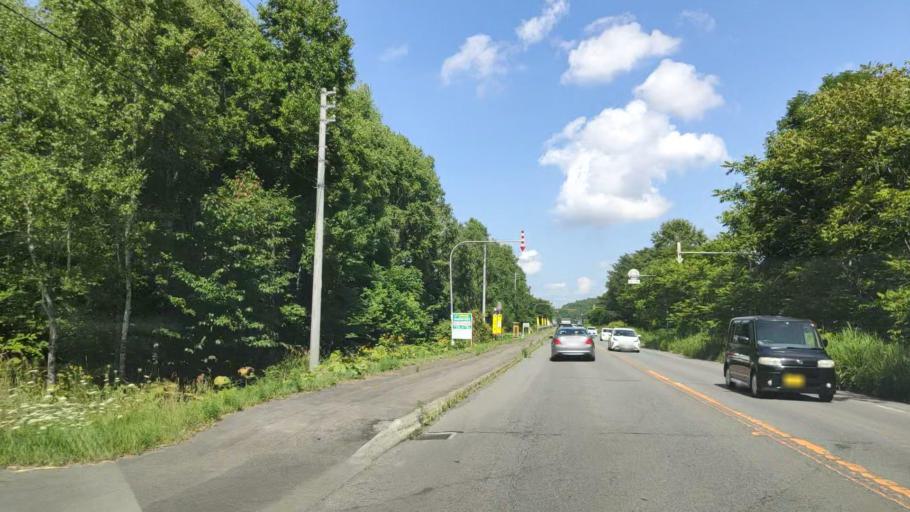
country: JP
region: Hokkaido
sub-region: Asahikawa-shi
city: Asahikawa
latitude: 43.6222
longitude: 142.4687
